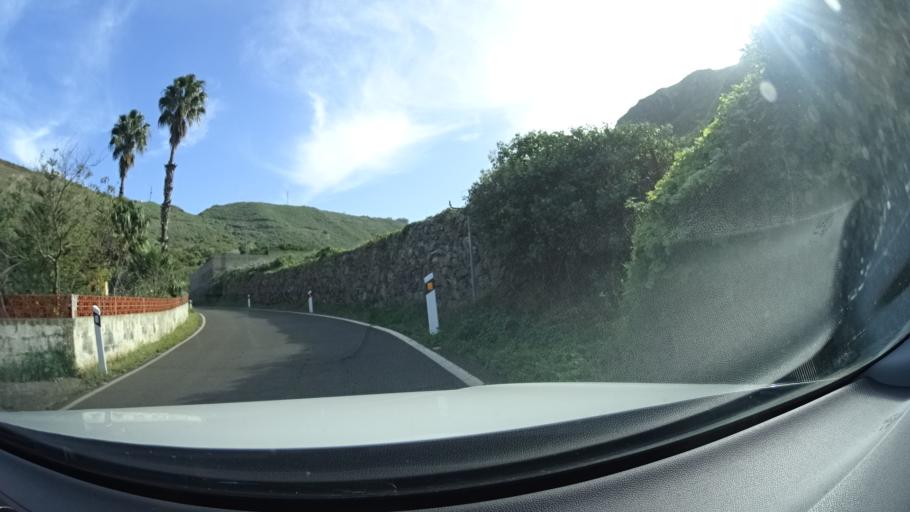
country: ES
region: Canary Islands
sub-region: Provincia de Las Palmas
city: Guia
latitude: 28.1088
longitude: -15.6415
